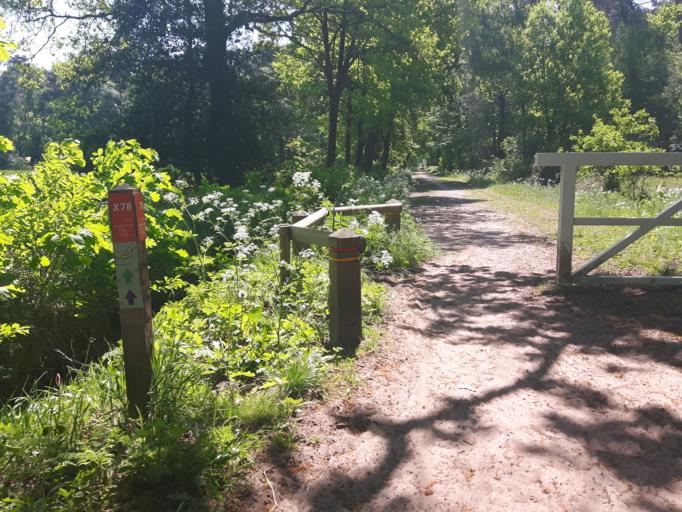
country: NL
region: Overijssel
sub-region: Gemeente Enschede
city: Enschede
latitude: 52.1747
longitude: 6.8695
